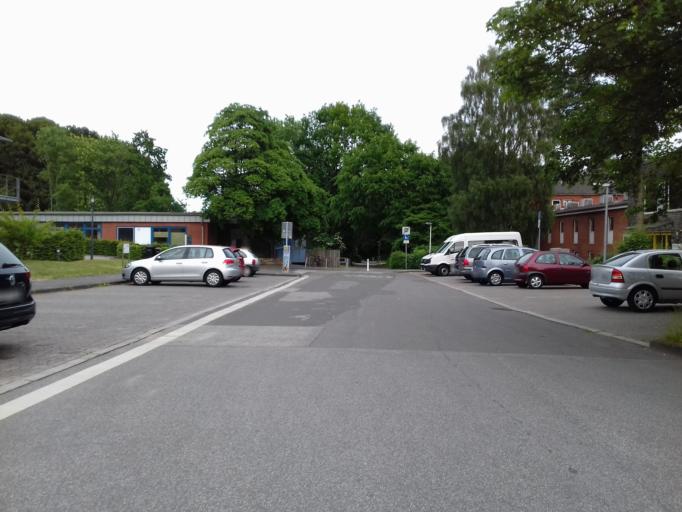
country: DE
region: Schleswig-Holstein
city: Kronshagen
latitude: 54.3190
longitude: 10.0705
